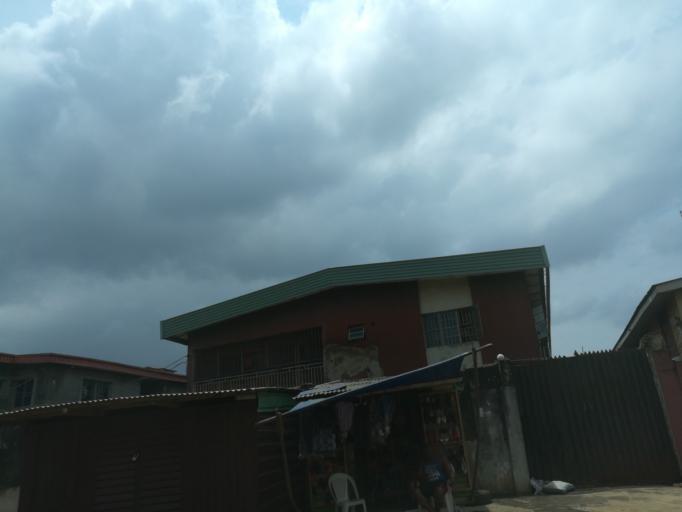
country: NG
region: Lagos
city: Oshodi
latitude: 6.5482
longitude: 3.3274
